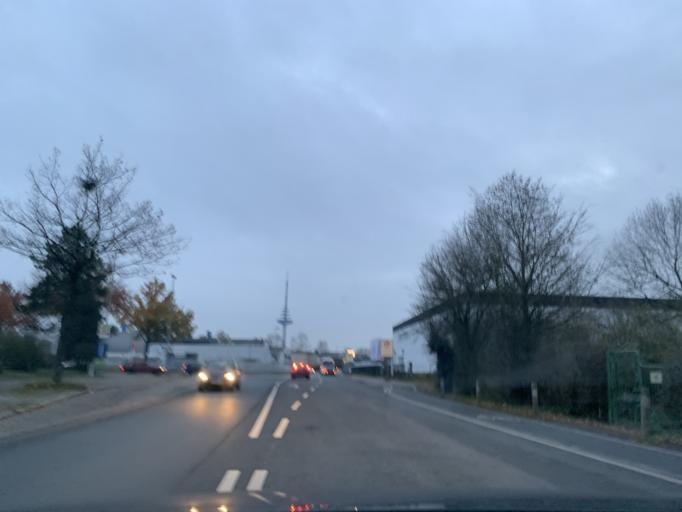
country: DE
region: Bremen
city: Bremen
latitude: 53.1069
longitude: 8.7960
